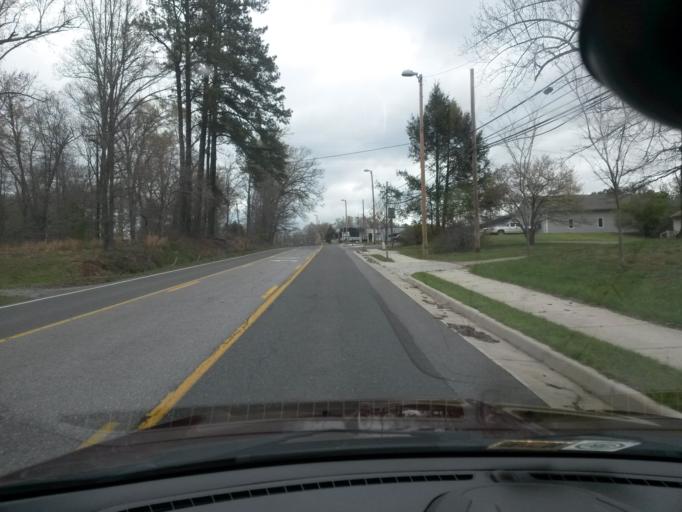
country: US
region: Virginia
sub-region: Amherst County
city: Amherst
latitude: 37.5741
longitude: -79.0580
